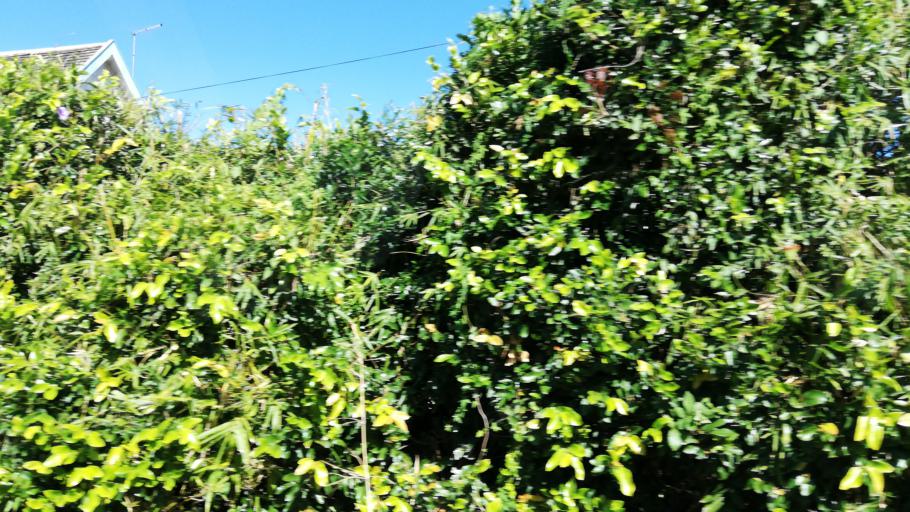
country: MU
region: Plaines Wilhems
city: Ebene
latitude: -20.2342
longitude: 57.4746
